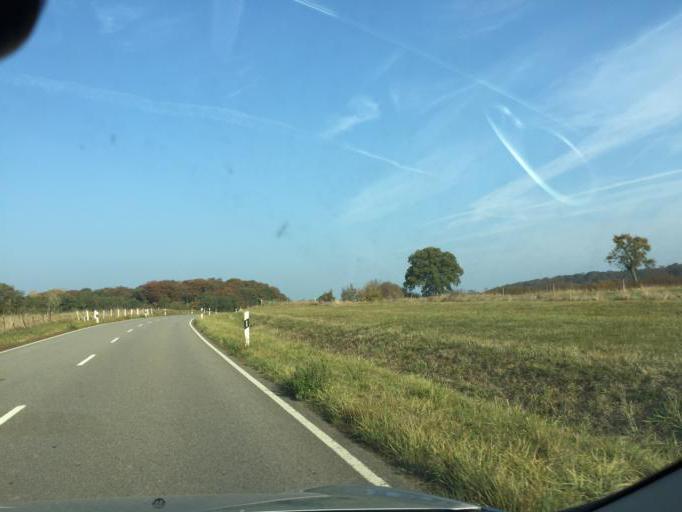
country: LU
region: Luxembourg
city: Aspelt
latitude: 49.5482
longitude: 6.2317
